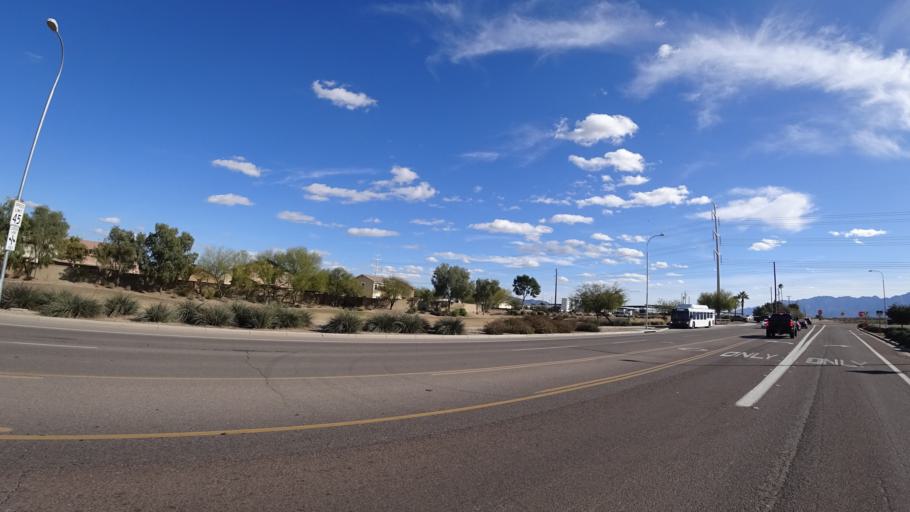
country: US
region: Arizona
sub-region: Maricopa County
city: Tolleson
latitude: 33.4096
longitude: -112.2214
